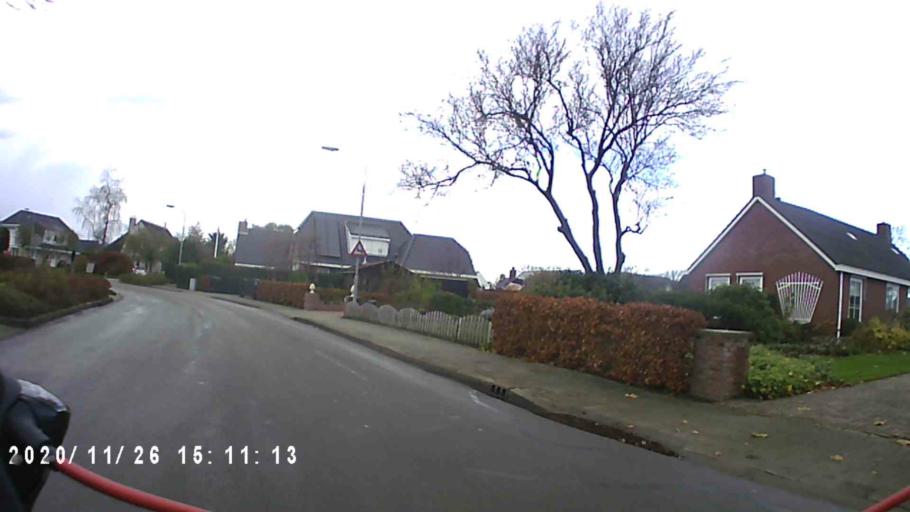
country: NL
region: Groningen
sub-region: Gemeente Appingedam
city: Appingedam
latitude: 53.3194
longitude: 6.8465
